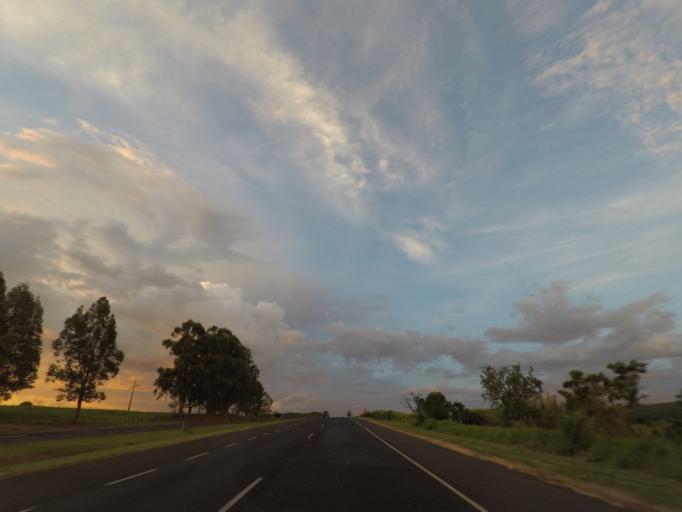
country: BR
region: Minas Gerais
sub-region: Uberaba
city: Uberaba
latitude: -19.6044
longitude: -48.0235
